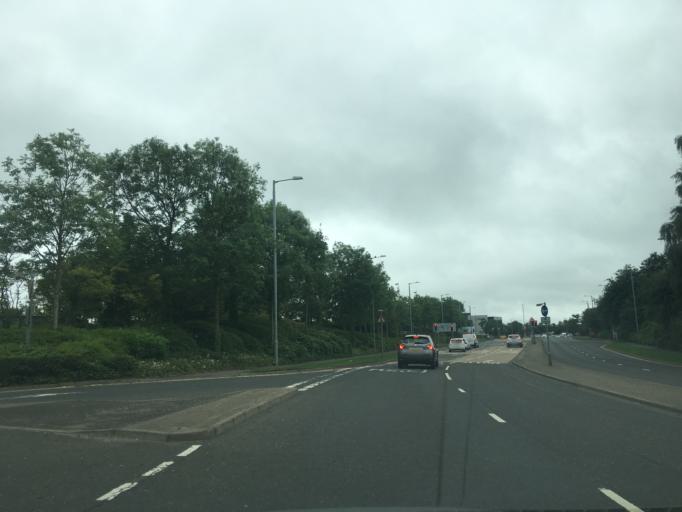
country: GB
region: Scotland
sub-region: Renfrewshire
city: Renfrew
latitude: 55.8756
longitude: -4.3684
